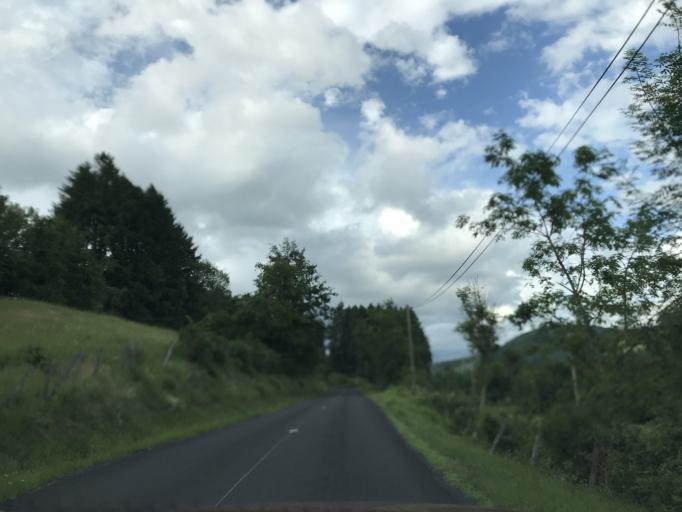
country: FR
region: Auvergne
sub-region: Departement du Puy-de-Dome
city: Escoutoux
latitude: 45.8123
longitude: 3.6124
